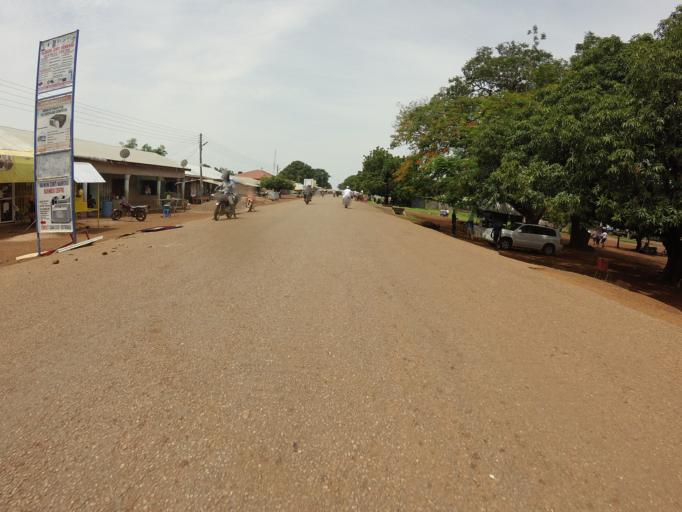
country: GH
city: Kpandae
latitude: 8.8598
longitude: 0.0552
